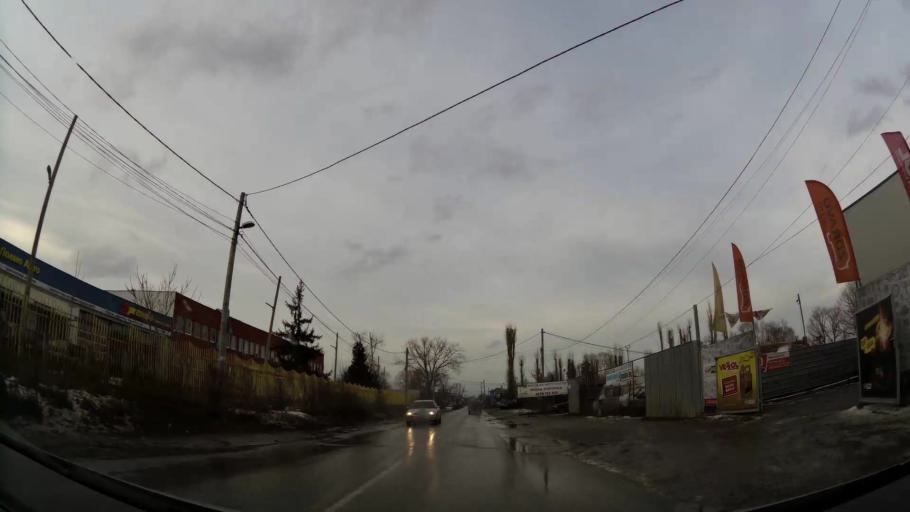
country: BG
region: Sofia-Capital
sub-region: Stolichna Obshtina
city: Sofia
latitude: 42.7294
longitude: 23.3442
